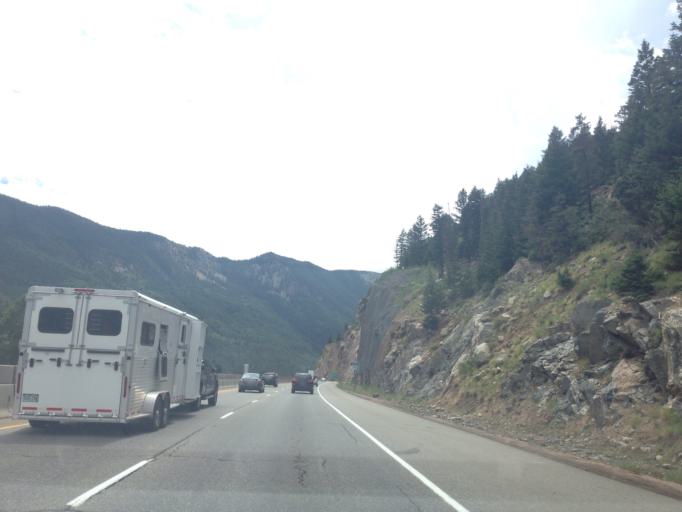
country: US
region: Colorado
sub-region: Clear Creek County
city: Georgetown
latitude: 39.7045
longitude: -105.7038
